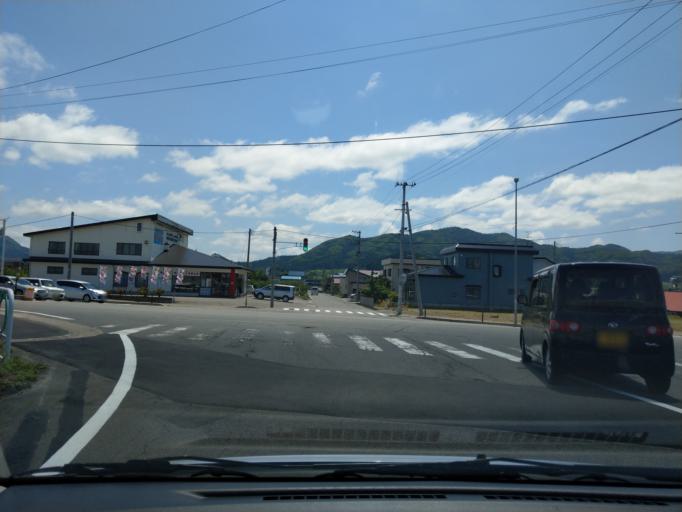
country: JP
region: Aomori
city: Hirosaki
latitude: 40.5545
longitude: 140.5494
